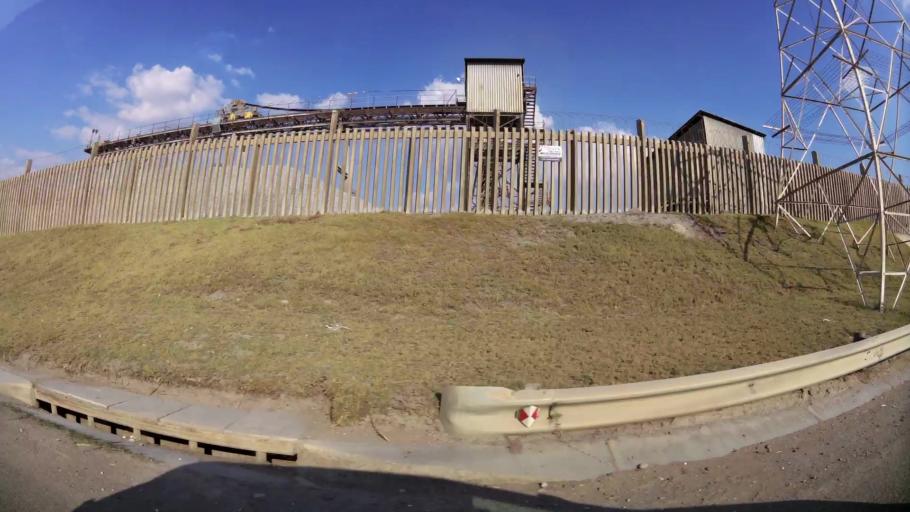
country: ZA
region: Gauteng
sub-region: Ekurhuleni Metropolitan Municipality
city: Tembisa
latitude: -25.9458
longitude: 28.2262
